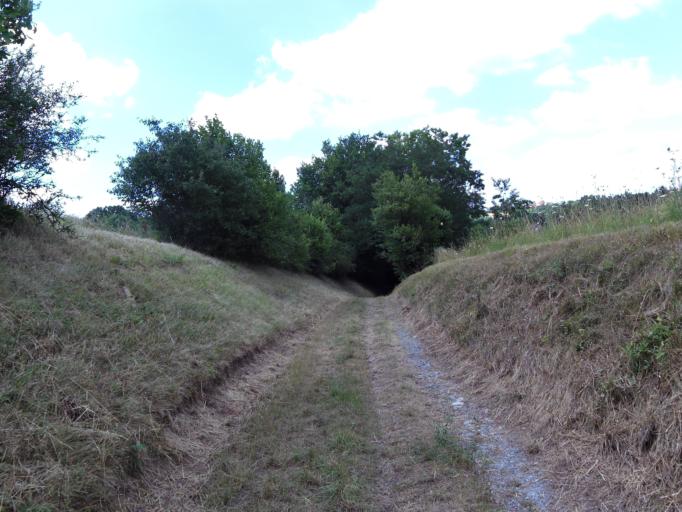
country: DE
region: Bavaria
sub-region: Regierungsbezirk Unterfranken
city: Gerbrunn
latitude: 49.7750
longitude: 9.9970
